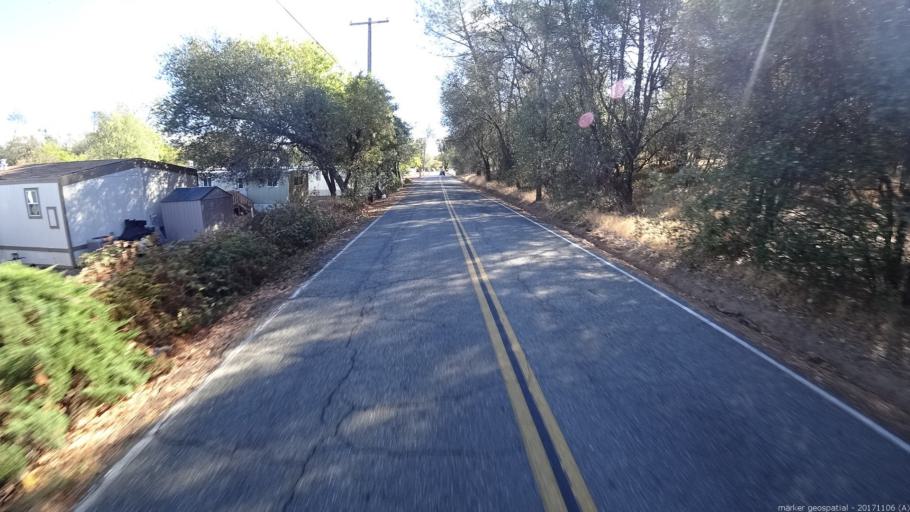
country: US
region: California
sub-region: Shasta County
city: Palo Cedro
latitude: 40.5824
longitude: -122.3031
